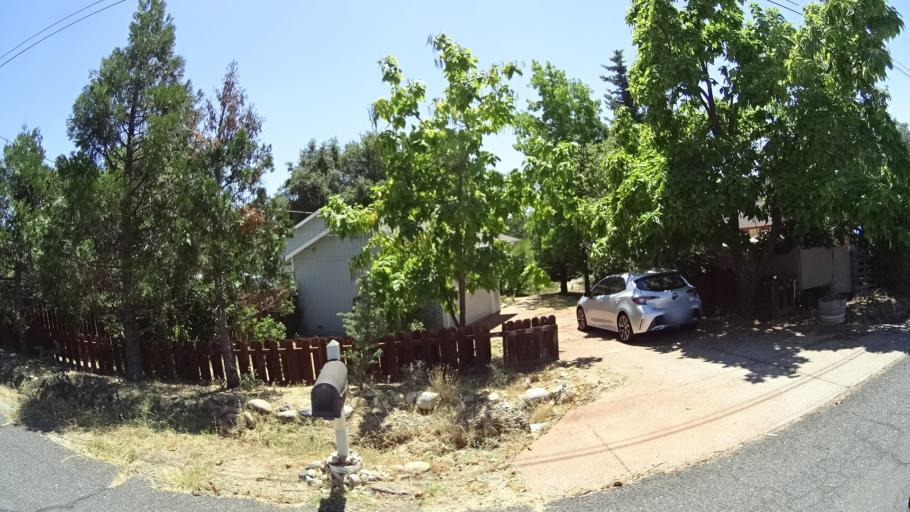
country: US
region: California
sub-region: Calaveras County
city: Angels Camp
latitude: 38.0947
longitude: -120.4999
